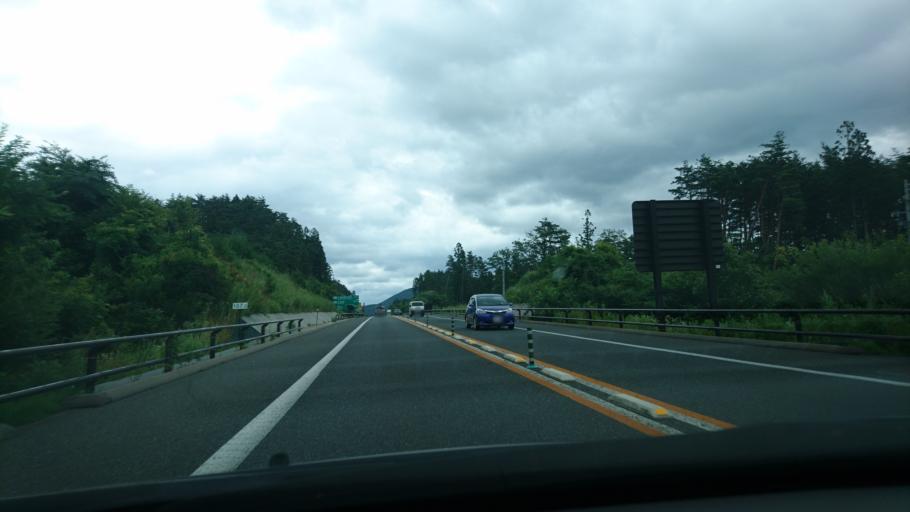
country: JP
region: Iwate
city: Ofunato
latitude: 39.0304
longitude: 141.6458
